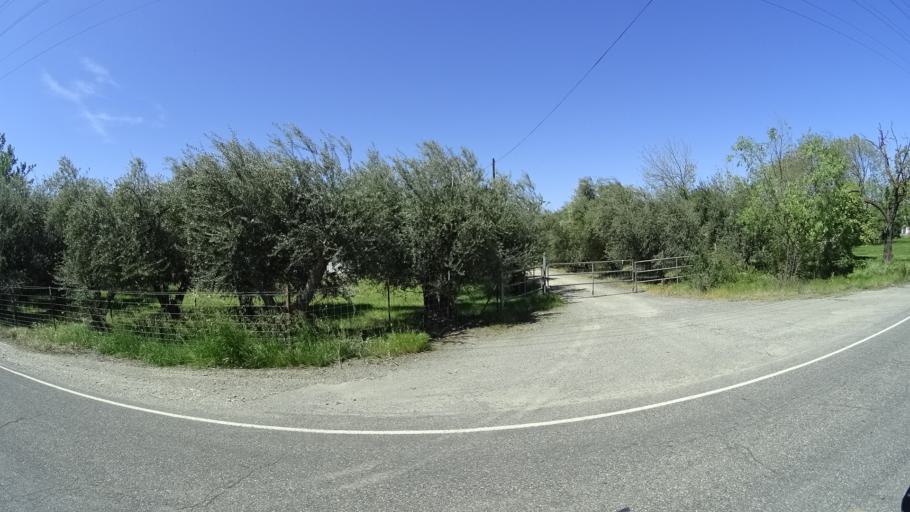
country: US
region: California
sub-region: Glenn County
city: Orland
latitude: 39.7190
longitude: -122.1784
